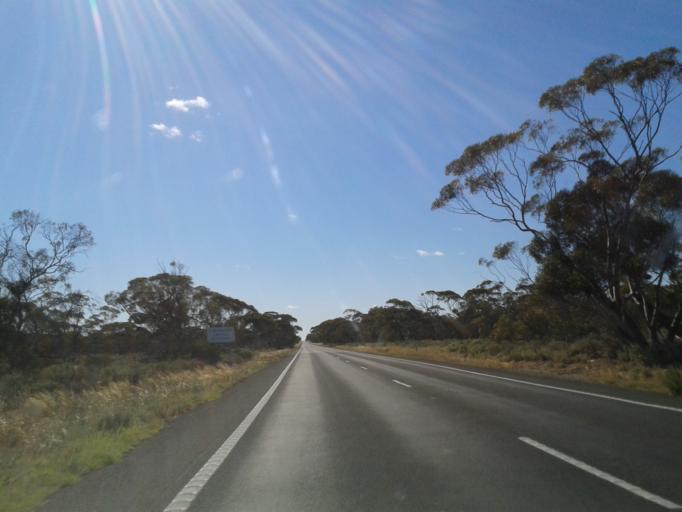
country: AU
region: South Australia
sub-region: Renmark Paringa
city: Renmark
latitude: -34.2744
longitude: 141.0091
